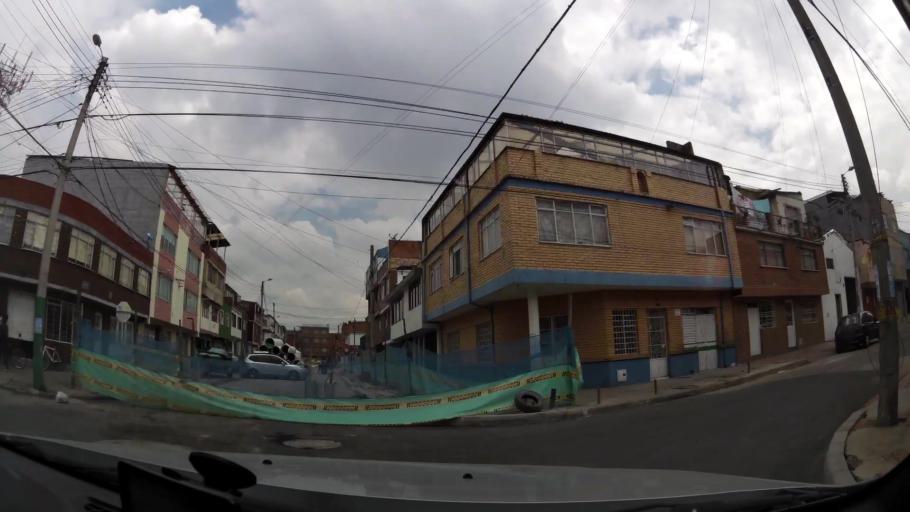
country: CO
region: Bogota D.C.
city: Barrio San Luis
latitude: 4.6811
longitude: -74.0663
